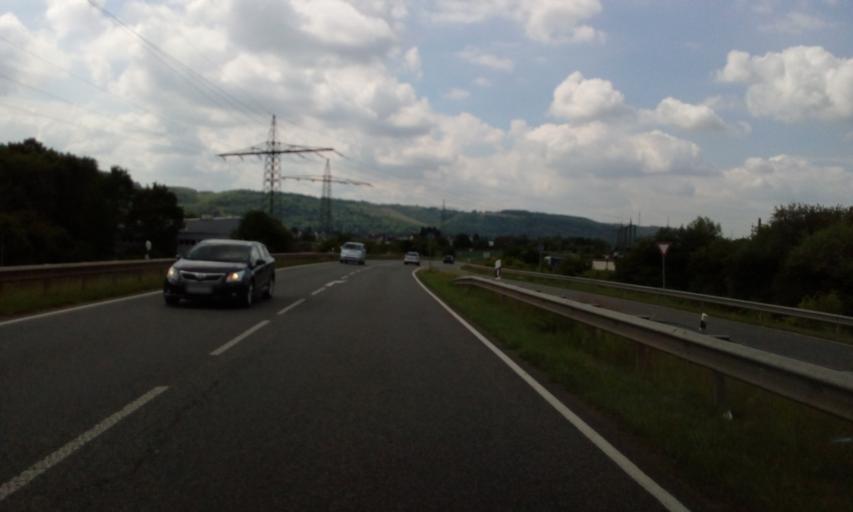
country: DE
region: Rheinland-Pfalz
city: Kenn
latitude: 49.7908
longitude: 6.6890
